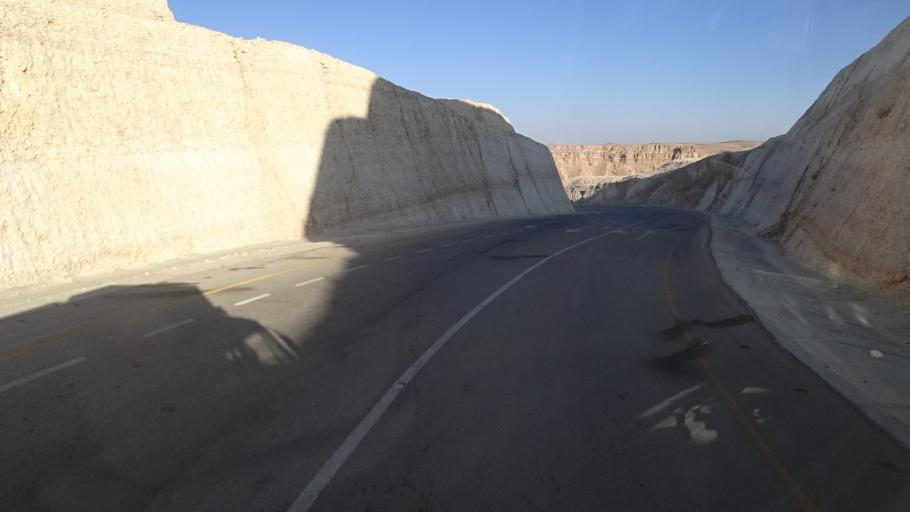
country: YE
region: Al Mahrah
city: Hawf
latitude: 17.0918
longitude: 53.0408
